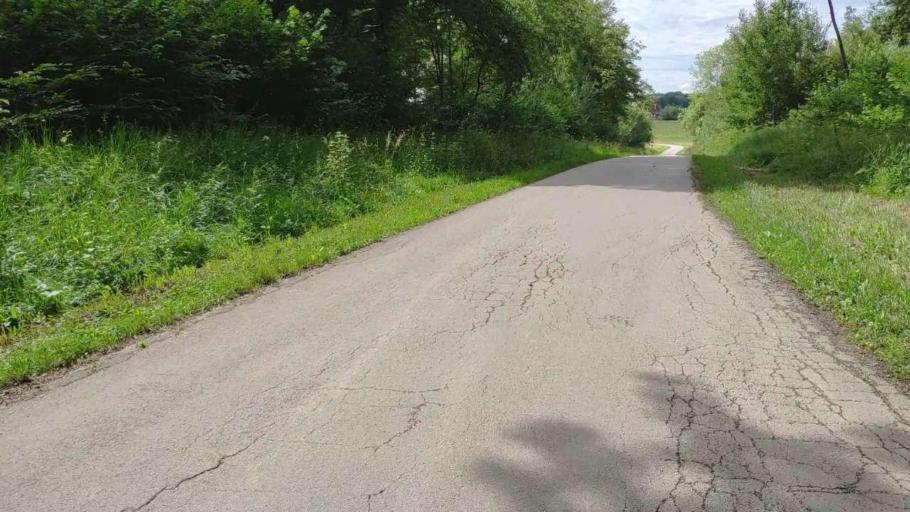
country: FR
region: Franche-Comte
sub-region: Departement du Jura
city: Bletterans
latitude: 46.8143
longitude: 5.4345
